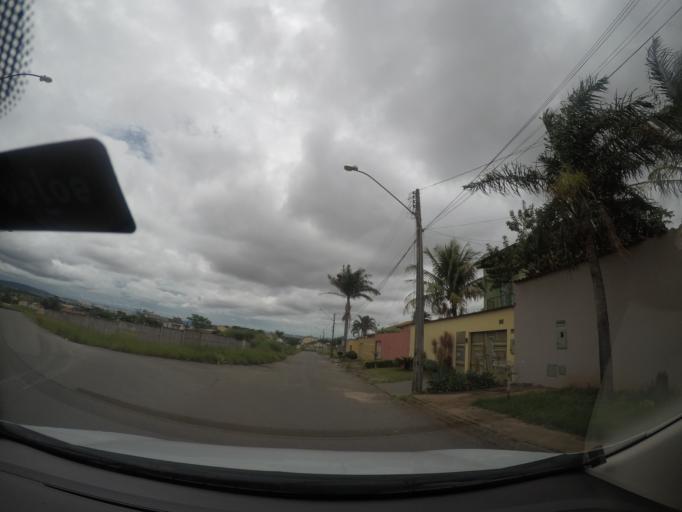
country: BR
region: Goias
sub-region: Goiania
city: Goiania
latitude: -16.7455
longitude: -49.3346
